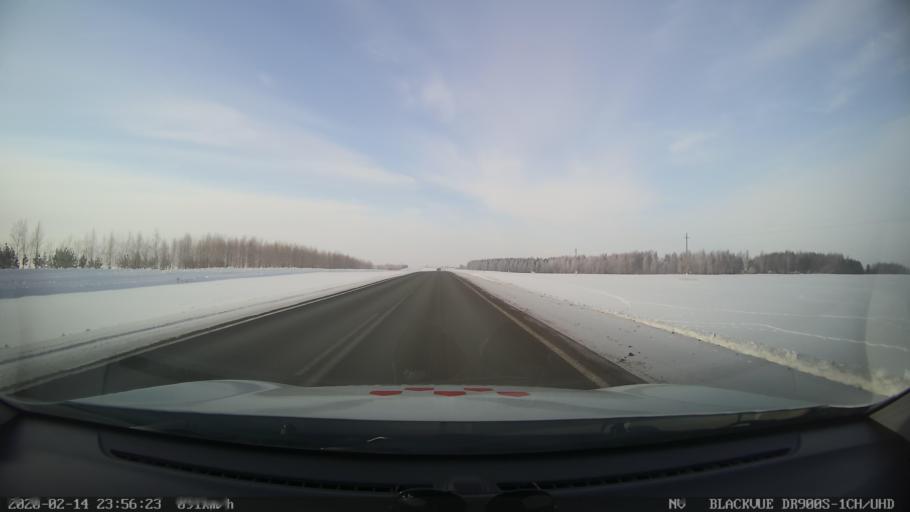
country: RU
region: Tatarstan
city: Kuybyshevskiy Zaton
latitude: 55.3241
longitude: 49.1309
